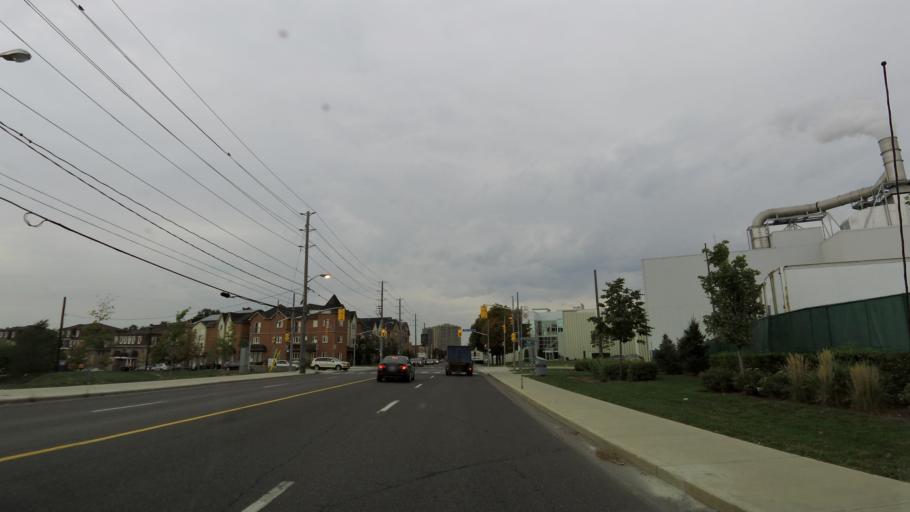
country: CA
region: Ontario
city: Etobicoke
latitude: 43.6929
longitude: -79.5041
